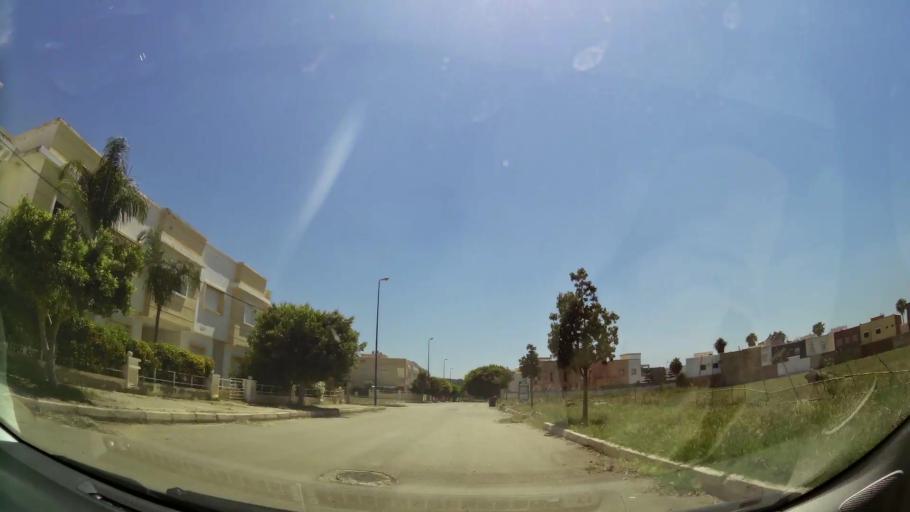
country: MA
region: Oriental
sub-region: Berkane-Taourirt
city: Madagh
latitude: 35.0726
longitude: -2.2166
